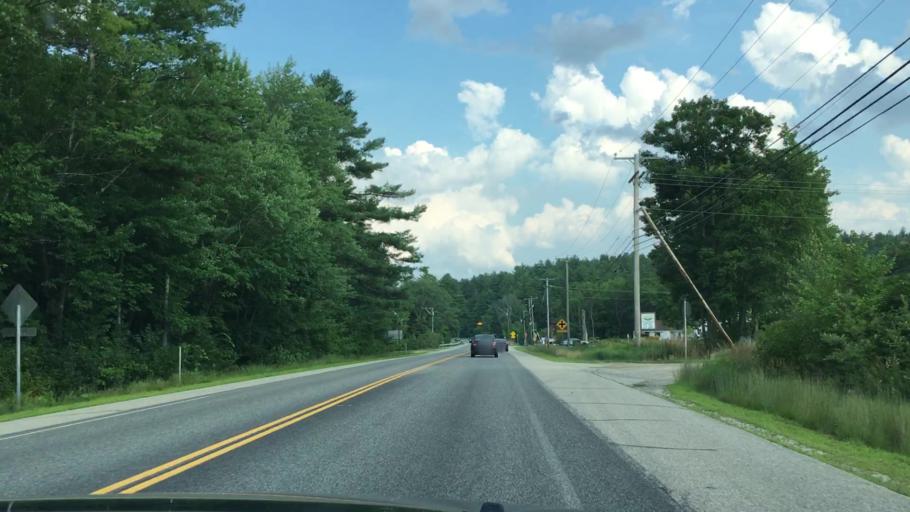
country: US
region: New Hampshire
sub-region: Strafford County
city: Farmington
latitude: 43.3881
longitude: -71.0842
